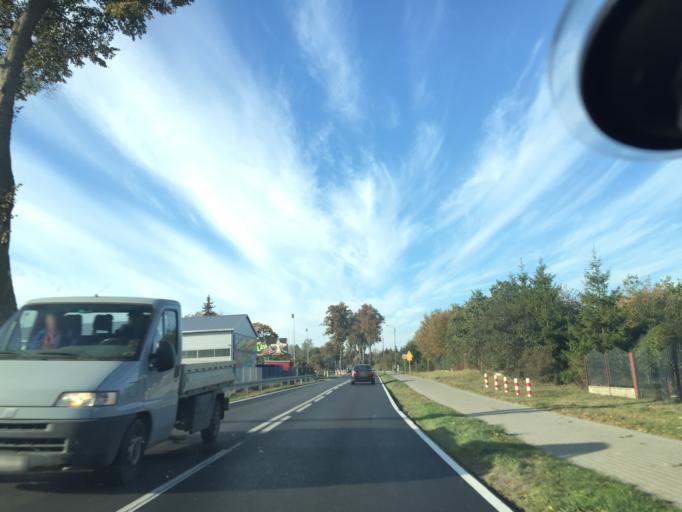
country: PL
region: Warmian-Masurian Voivodeship
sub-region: Powiat lidzbarski
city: Lidzbark Warminski
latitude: 54.1291
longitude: 20.6026
